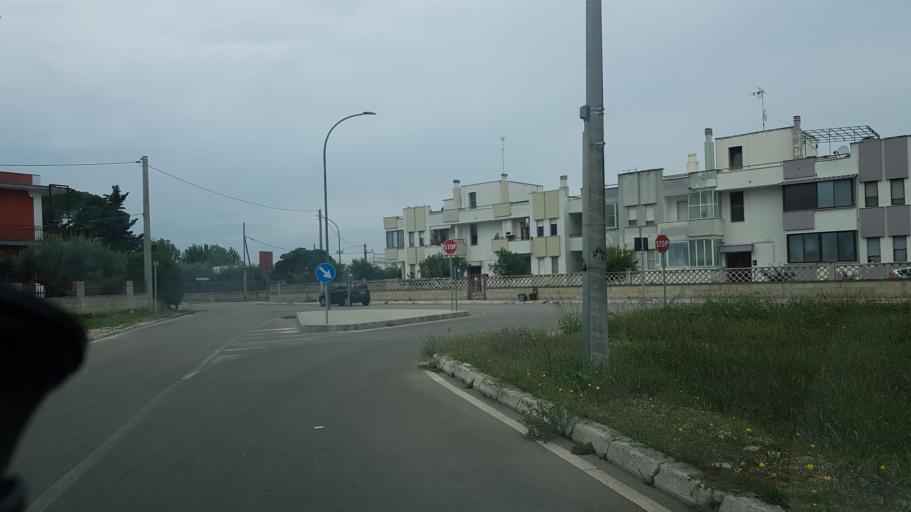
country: IT
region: Apulia
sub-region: Provincia di Lecce
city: Guagnano
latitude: 40.4000
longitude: 17.9422
